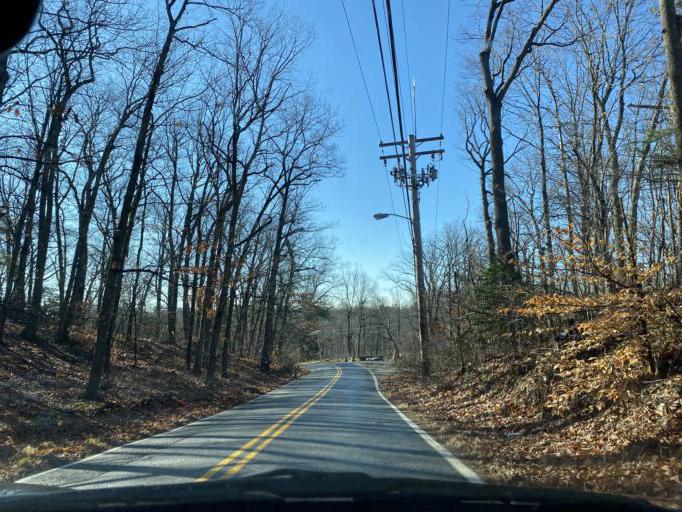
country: US
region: Maryland
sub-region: Prince George's County
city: West Laurel
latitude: 39.0921
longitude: -76.8849
